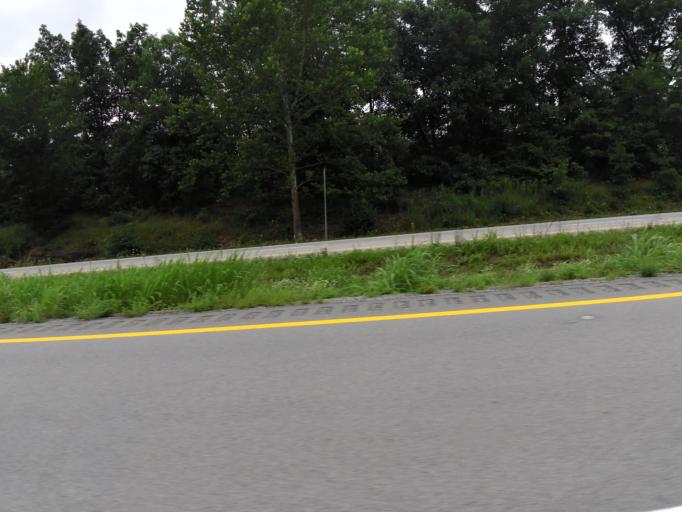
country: US
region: Kentucky
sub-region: Grayson County
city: Leitchfield
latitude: 37.4131
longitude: -86.5119
